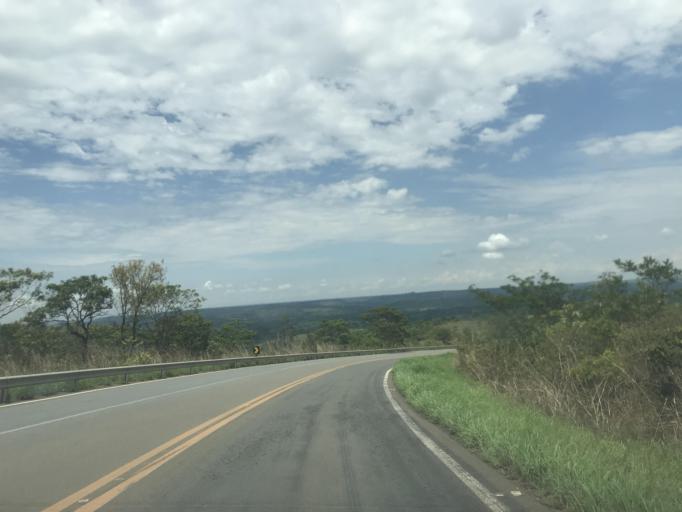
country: BR
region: Goias
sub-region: Luziania
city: Luziania
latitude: -16.3515
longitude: -48.0423
